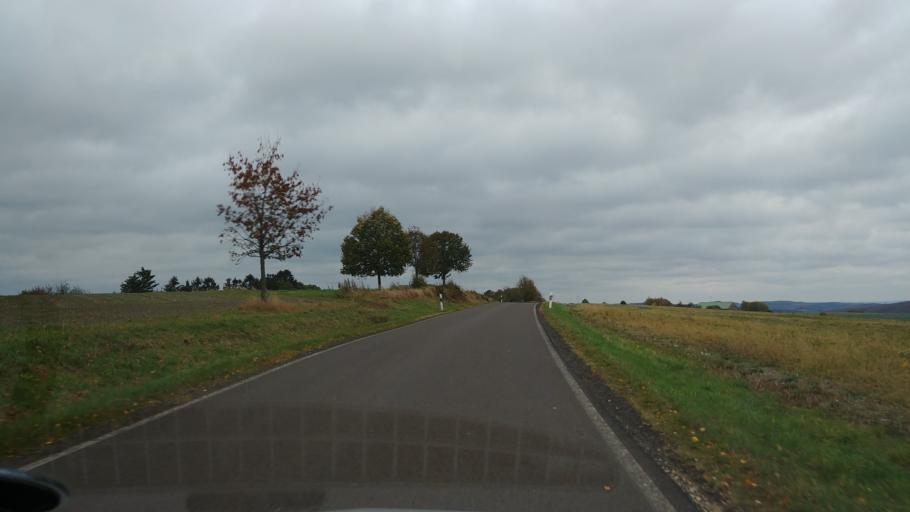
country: DE
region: Rheinland-Pfalz
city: Rorodt
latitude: 49.7851
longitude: 7.0721
